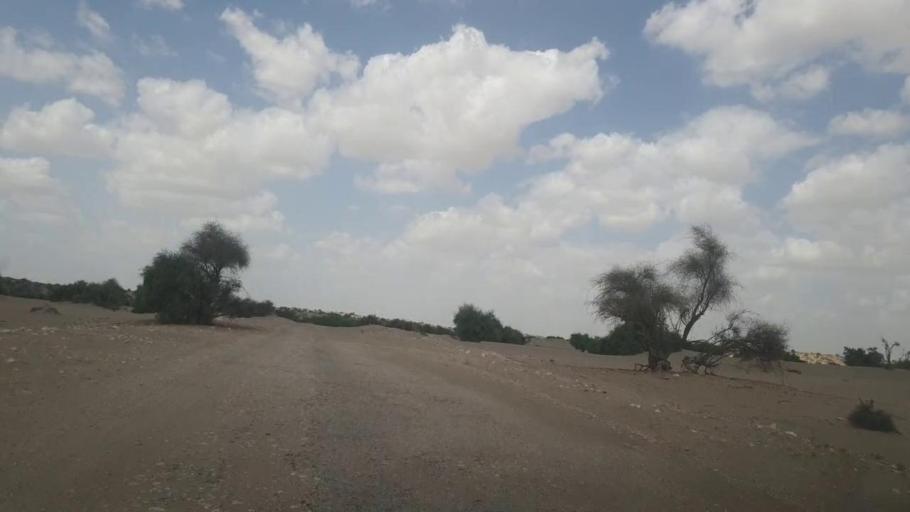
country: PK
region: Sindh
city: Kot Diji
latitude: 27.2808
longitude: 69.2257
